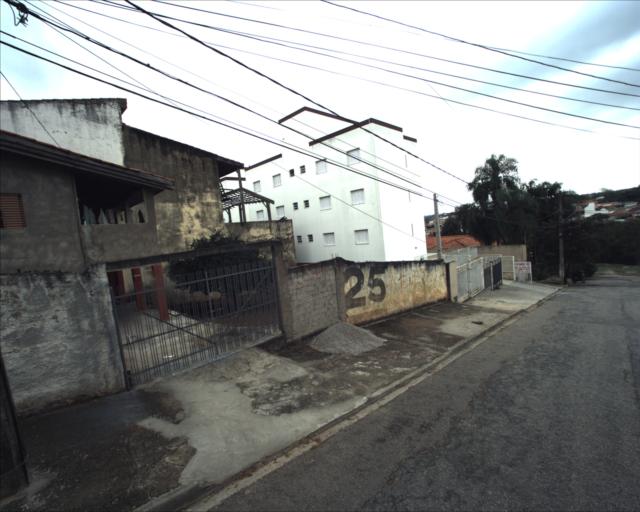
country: BR
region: Sao Paulo
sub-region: Sorocaba
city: Sorocaba
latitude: -23.4987
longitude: -47.4948
